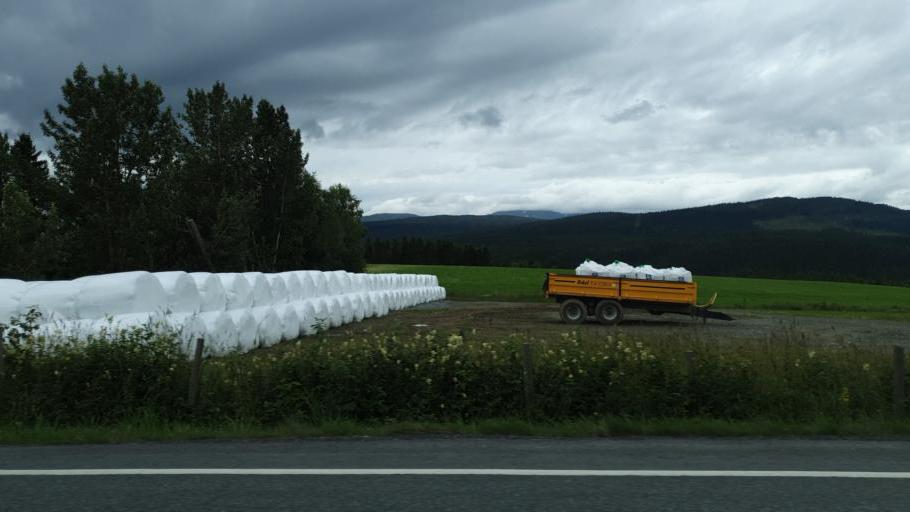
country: NO
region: Sor-Trondelag
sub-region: Rennebu
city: Berkak
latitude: 62.8064
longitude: 10.0337
